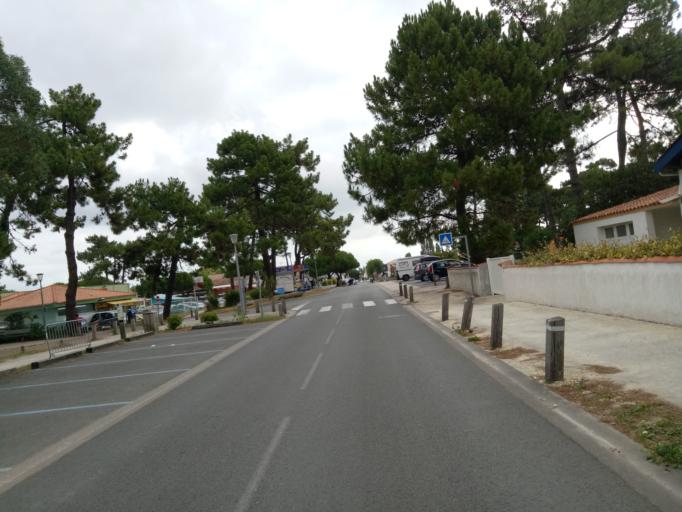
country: FR
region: Poitou-Charentes
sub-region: Departement de la Charente-Maritime
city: Saint-Trojan-les-Bains
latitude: 45.8603
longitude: -1.2401
